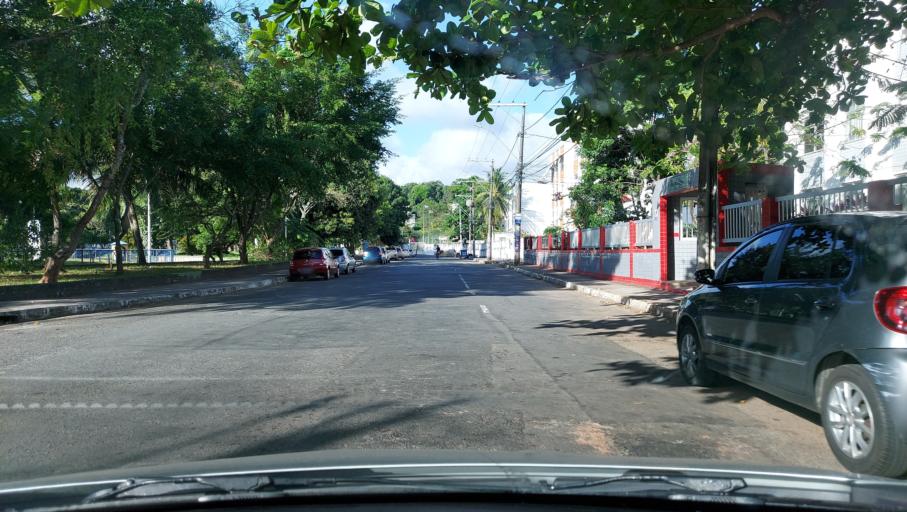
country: BR
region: Bahia
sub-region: Salvador
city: Salvador
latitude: -12.9800
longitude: -38.4481
